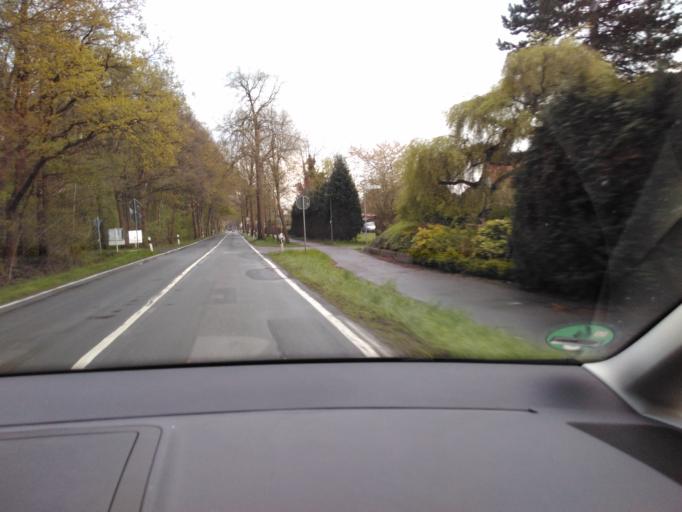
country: DE
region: North Rhine-Westphalia
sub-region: Regierungsbezirk Detmold
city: Verl
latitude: 51.9039
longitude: 8.4968
